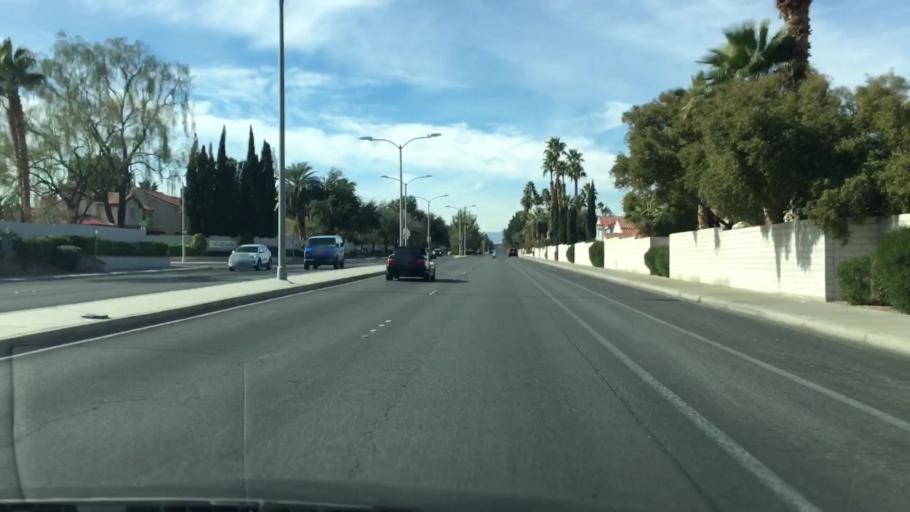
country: US
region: Nevada
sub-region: Clark County
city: Whitney
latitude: 36.0563
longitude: -115.0696
